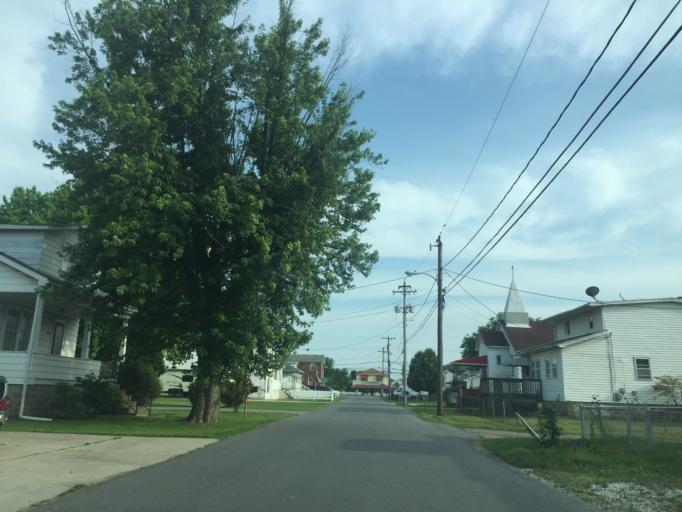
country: US
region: Maryland
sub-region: Baltimore County
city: Edgemere
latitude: 39.2338
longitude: -76.4561
